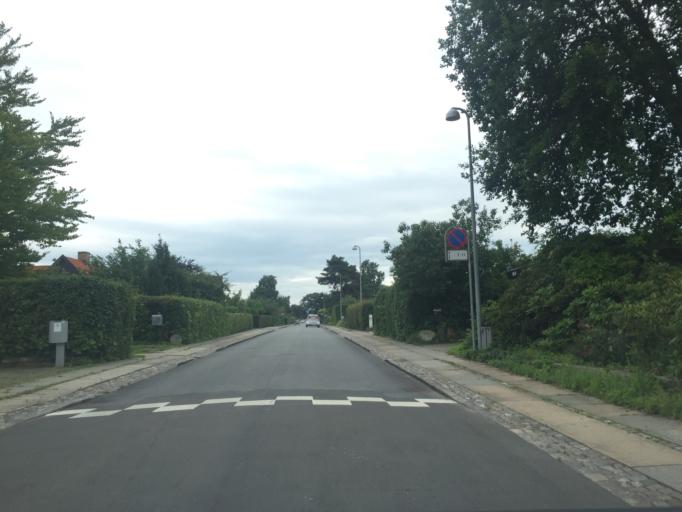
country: DK
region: Capital Region
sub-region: Lyngby-Tarbaek Kommune
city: Kongens Lyngby
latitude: 55.7936
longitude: 12.5418
